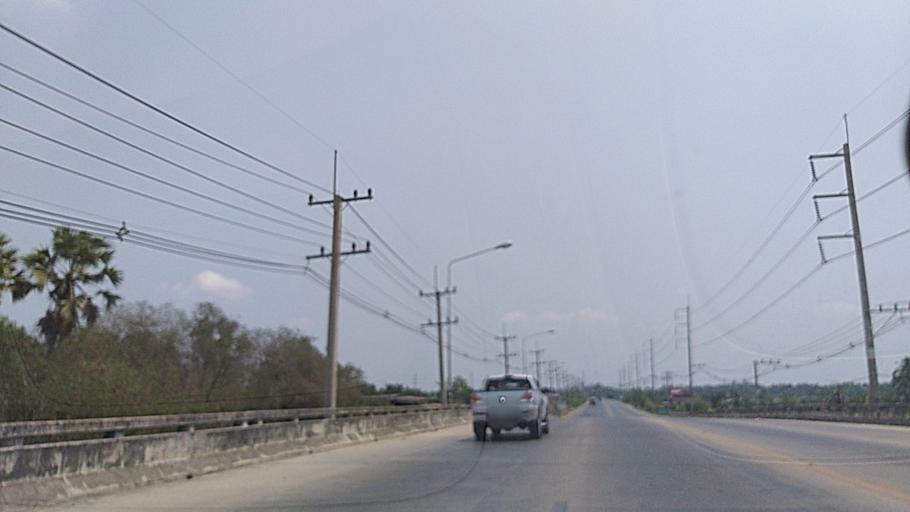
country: TH
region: Bangkok
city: Nong Chok
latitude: 13.9643
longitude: 100.9141
